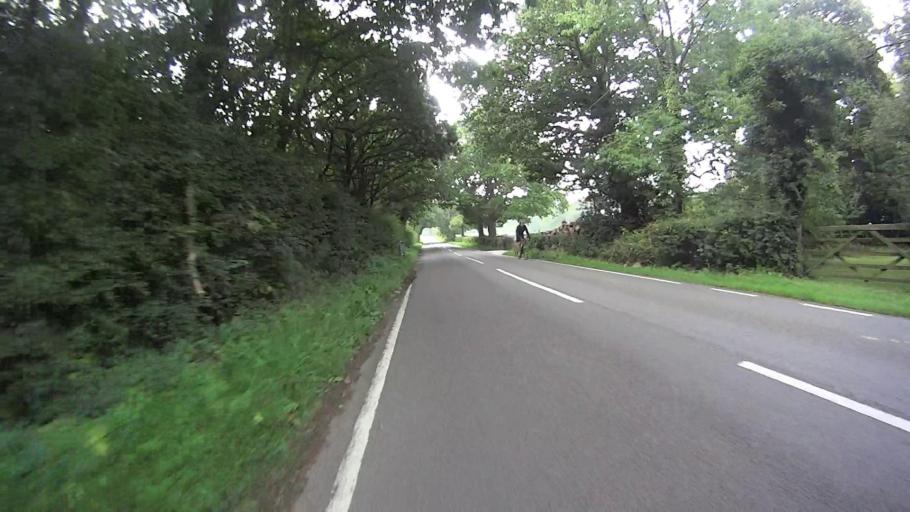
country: GB
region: England
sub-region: West Sussex
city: Copthorne
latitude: 51.1519
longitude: -0.1108
